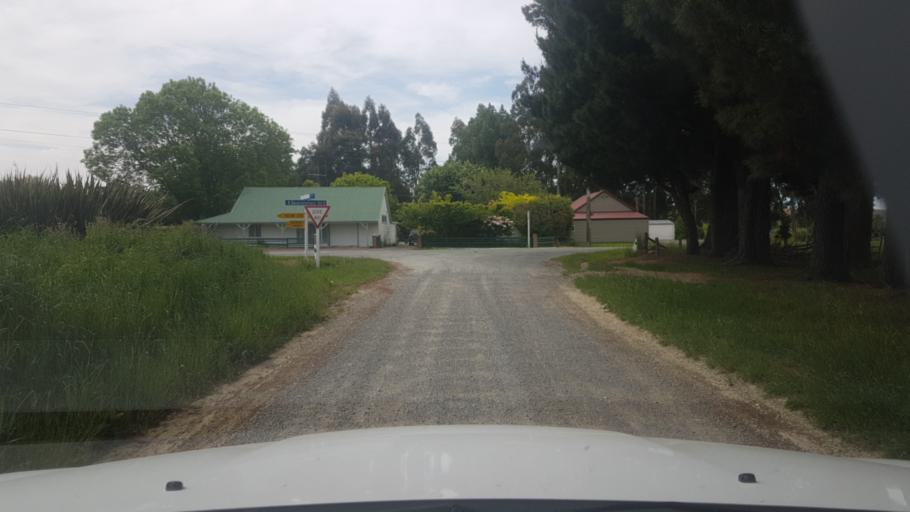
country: NZ
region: Canterbury
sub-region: Timaru District
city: Timaru
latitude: -44.4402
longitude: 171.1622
